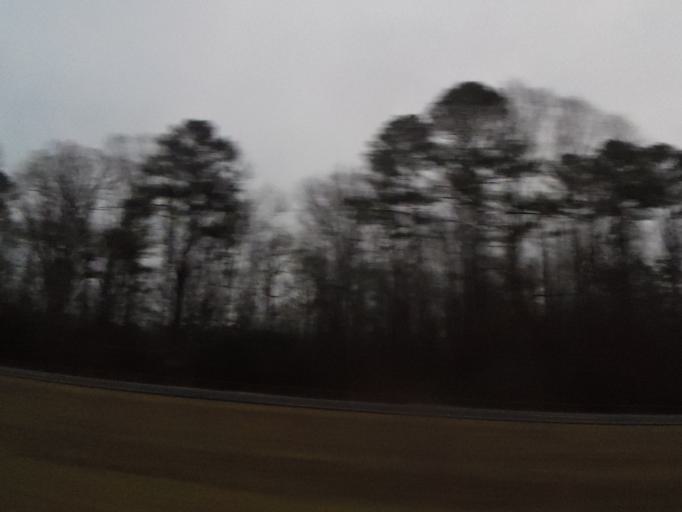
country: US
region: Alabama
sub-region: Morgan County
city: Falkville
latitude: 34.2655
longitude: -86.8971
